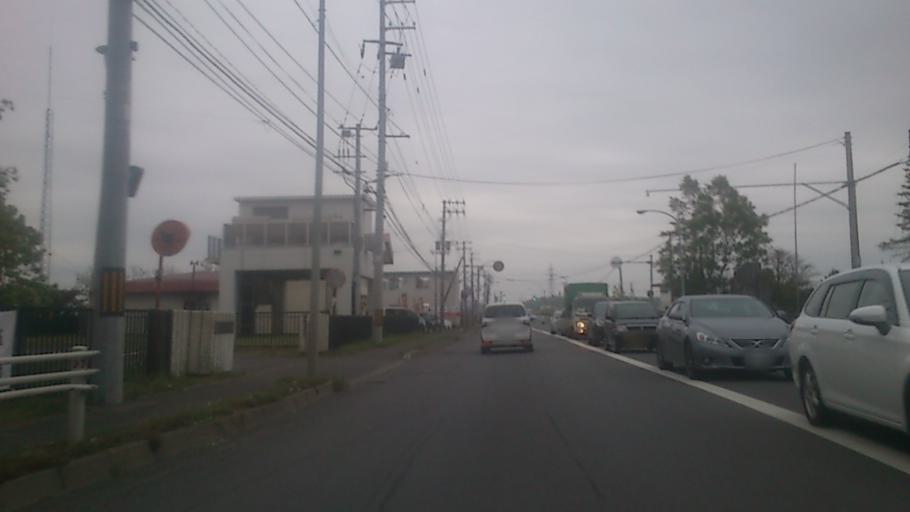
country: JP
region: Hokkaido
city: Kushiro
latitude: 42.9981
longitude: 144.4115
